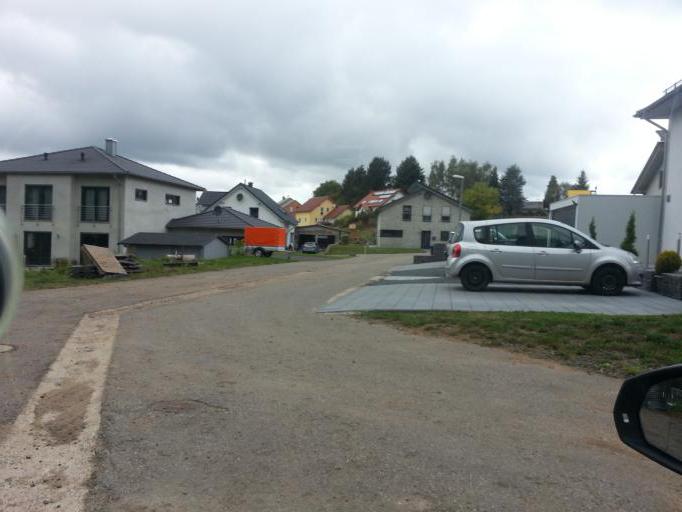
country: DE
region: Saarland
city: Freisen
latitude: 49.5472
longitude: 7.2460
